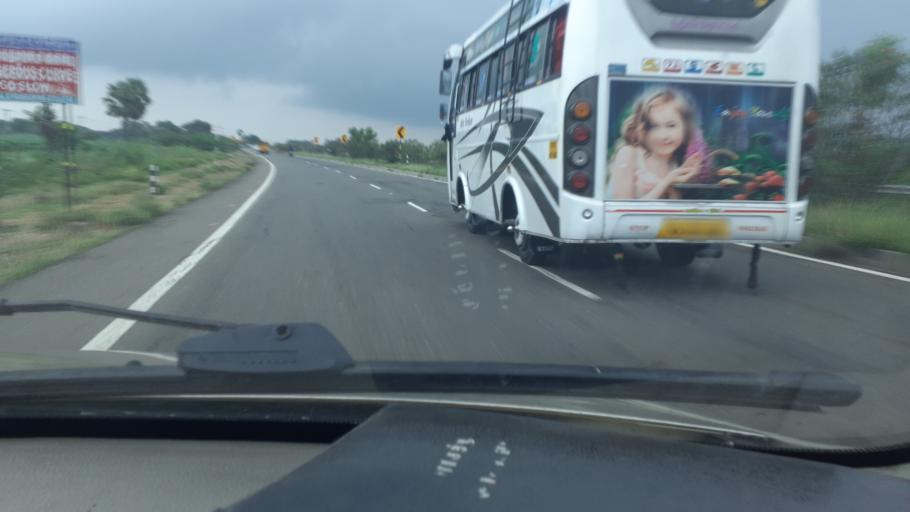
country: IN
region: Tamil Nadu
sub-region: Thoothukkudi
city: Kovilpatti
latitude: 9.1326
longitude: 77.8251
